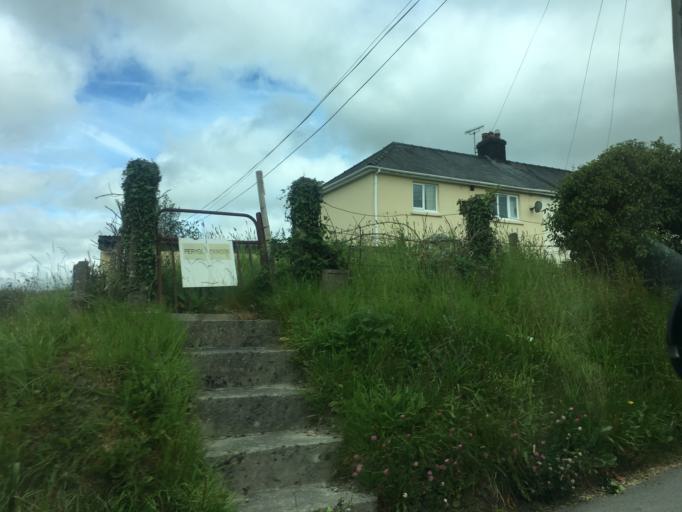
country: GB
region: Wales
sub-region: County of Ceredigion
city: Lampeter
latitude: 52.1019
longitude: -4.0609
